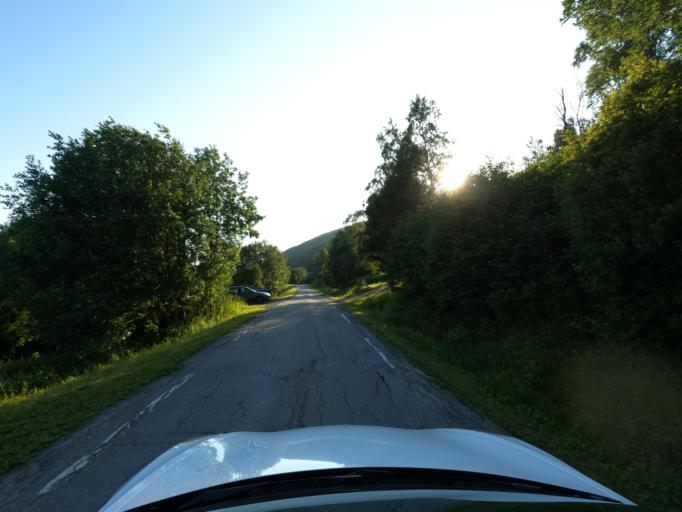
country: NO
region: Nordland
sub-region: Ballangen
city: Ballangen
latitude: 68.4678
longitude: 16.7928
